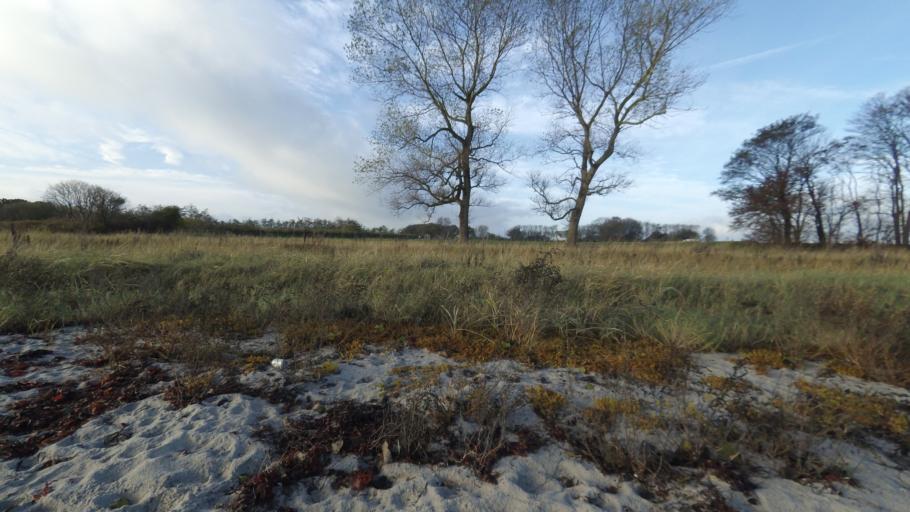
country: DK
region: Central Jutland
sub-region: Odder Kommune
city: Odder
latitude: 55.9287
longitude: 10.2578
